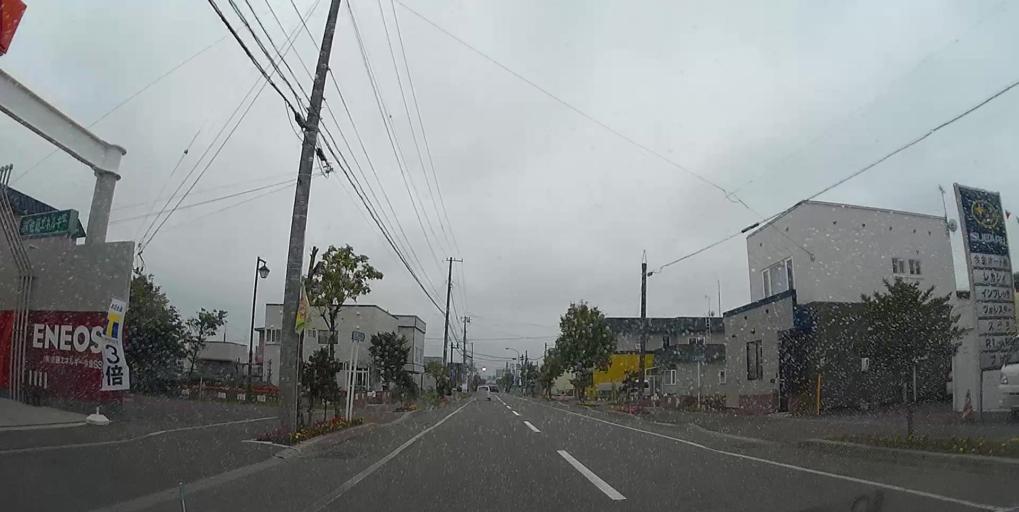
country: JP
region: Hokkaido
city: Iwanai
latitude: 42.4275
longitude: 140.0081
